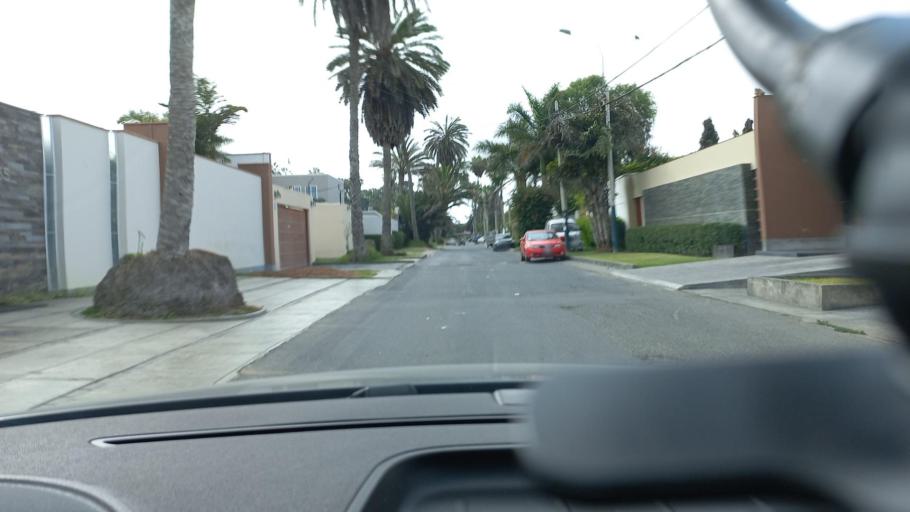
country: PE
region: Lima
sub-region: Lima
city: Surco
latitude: -12.2082
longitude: -77.0077
